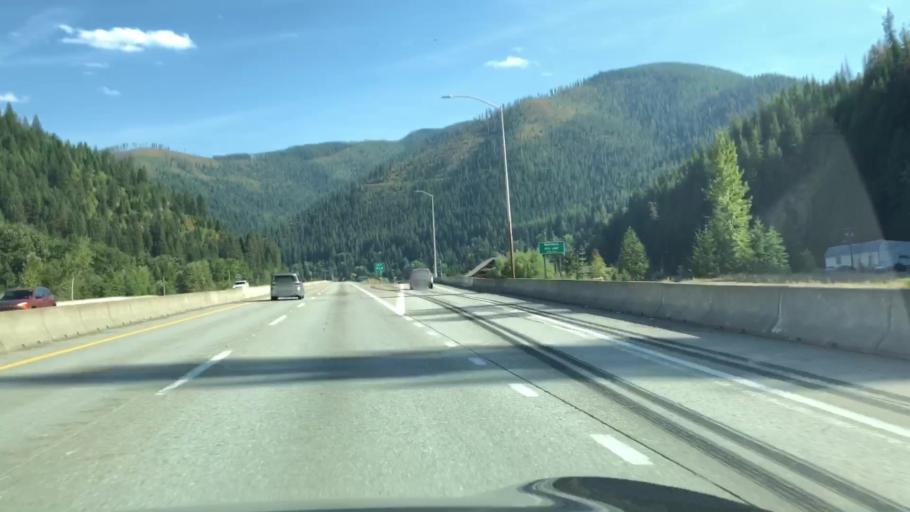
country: US
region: Idaho
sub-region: Shoshone County
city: Wallace
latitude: 47.4803
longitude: -115.9358
